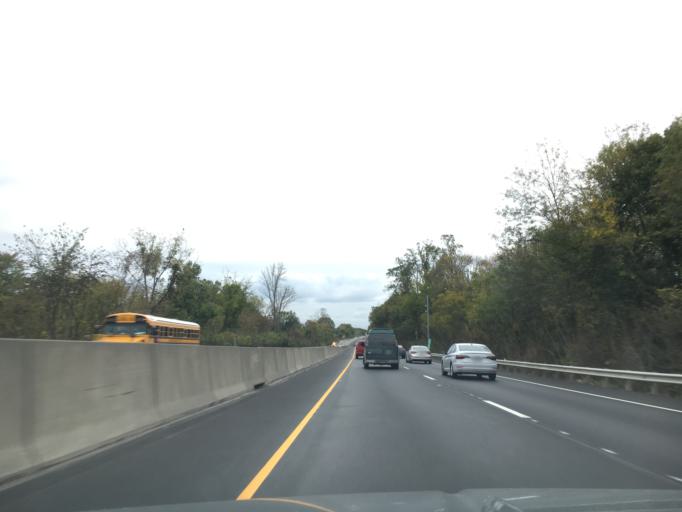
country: US
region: Pennsylvania
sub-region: Chester County
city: Downingtown
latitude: 40.0170
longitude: -75.7092
